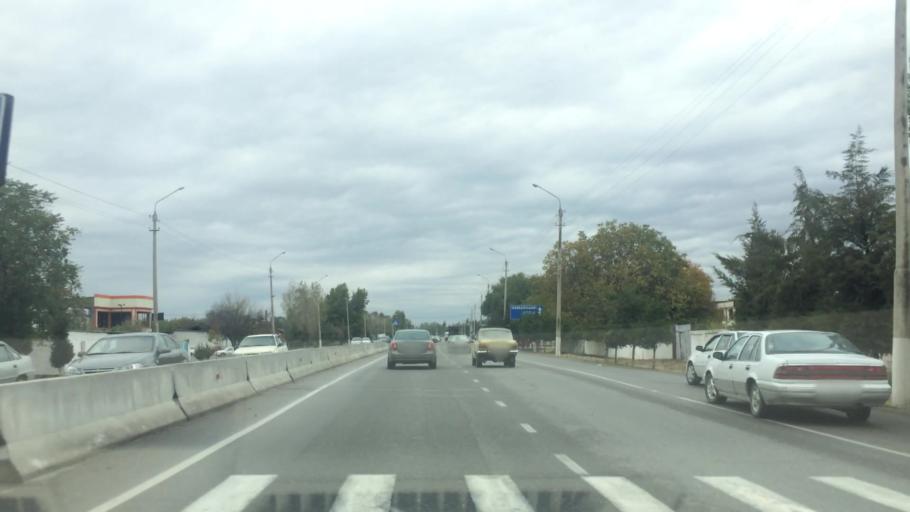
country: UZ
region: Jizzax
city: Jizzax
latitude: 40.0004
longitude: 67.5910
